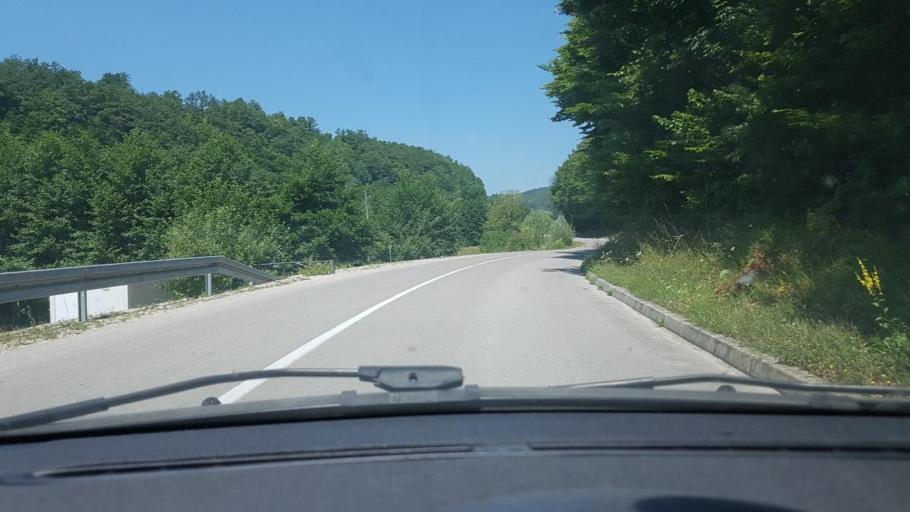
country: BA
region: Federation of Bosnia and Herzegovina
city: Orasac
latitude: 44.5527
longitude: 16.1053
